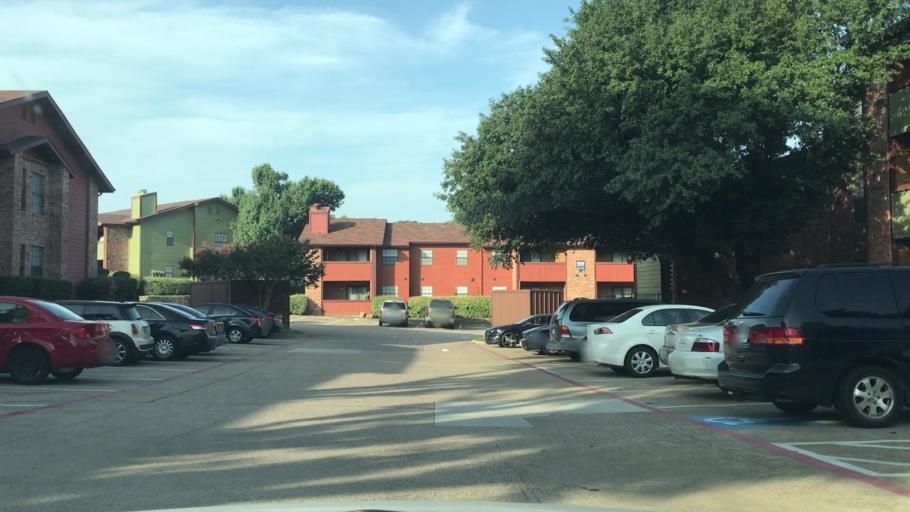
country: US
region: Texas
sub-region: Tarrant County
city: Pantego
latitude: 32.7615
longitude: -97.1619
